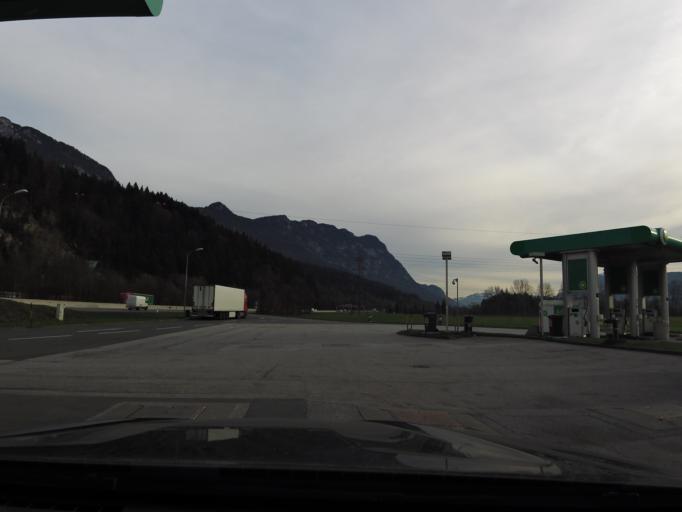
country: AT
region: Tyrol
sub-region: Politischer Bezirk Kufstein
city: Angath
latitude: 47.5180
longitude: 12.0671
